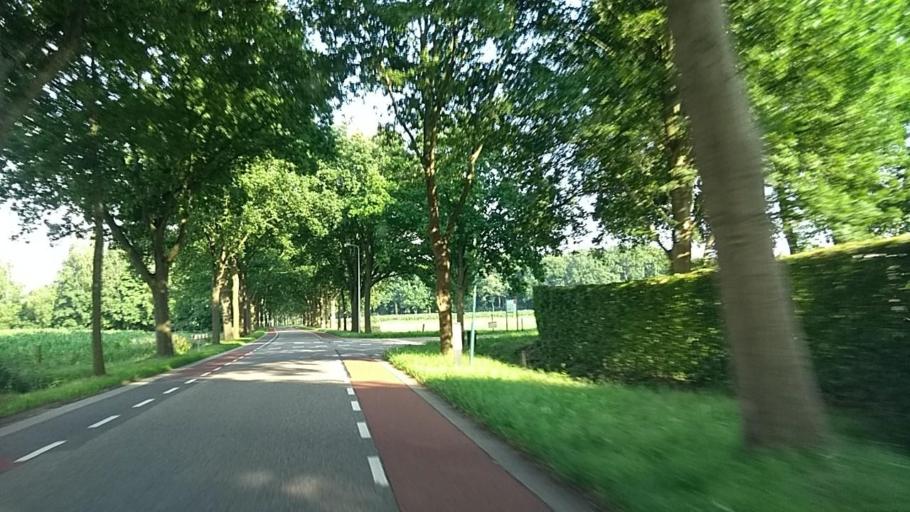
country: NL
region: Overijssel
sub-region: Gemeente Zwolle
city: Zwolle
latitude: 52.5444
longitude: 6.1360
